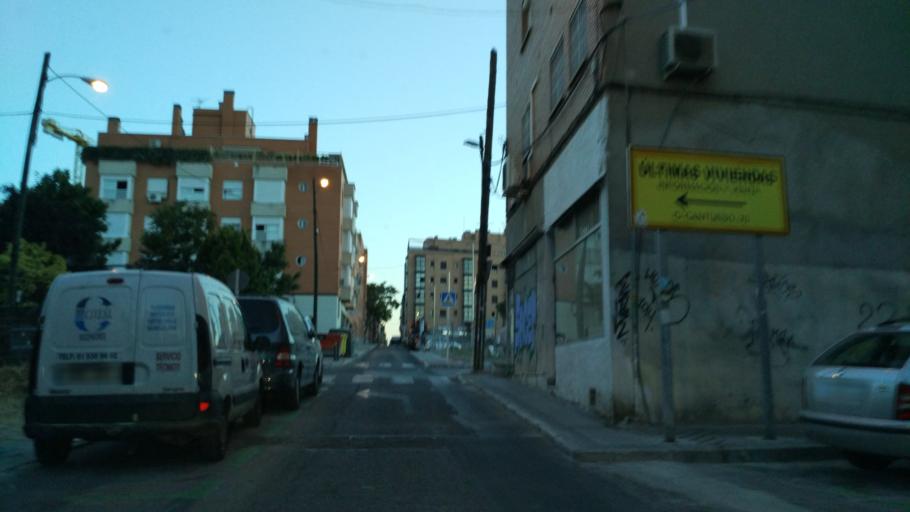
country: ES
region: Madrid
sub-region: Provincia de Madrid
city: Tetuan de las Victorias
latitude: 40.4684
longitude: -3.7041
